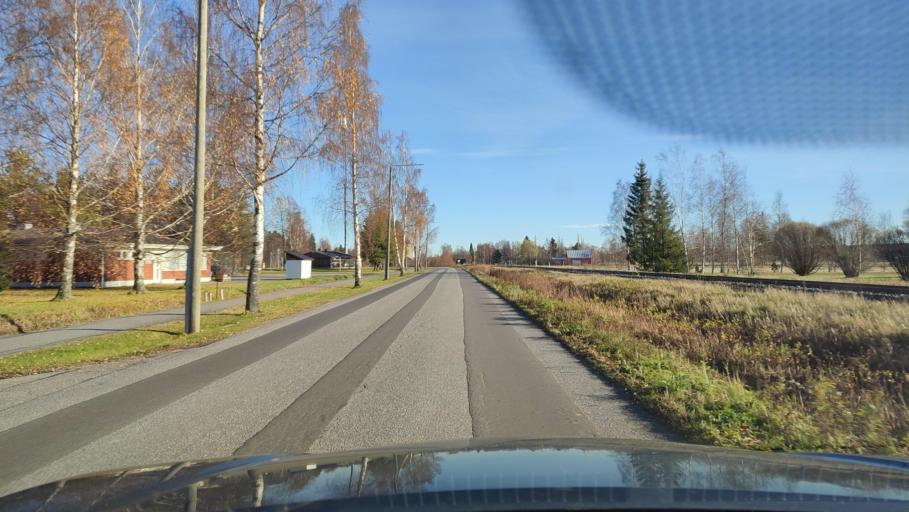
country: FI
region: Southern Ostrobothnia
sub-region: Suupohja
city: Teuva
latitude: 62.4719
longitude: 21.7272
